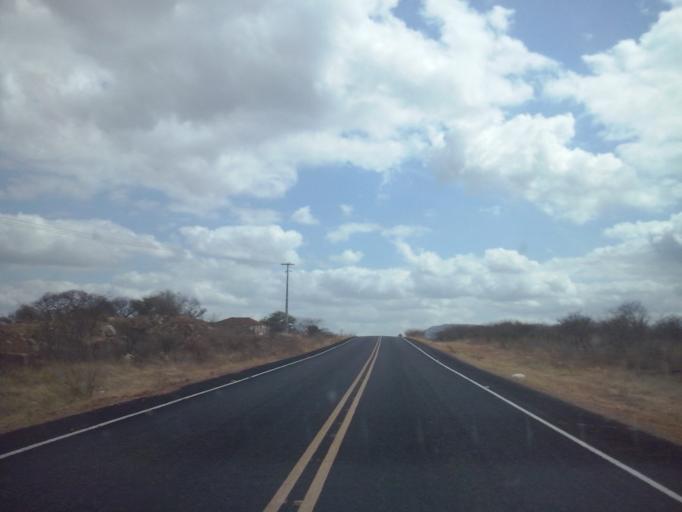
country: BR
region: Paraiba
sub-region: Pombal
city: Pombal
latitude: -6.8319
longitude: -37.5685
